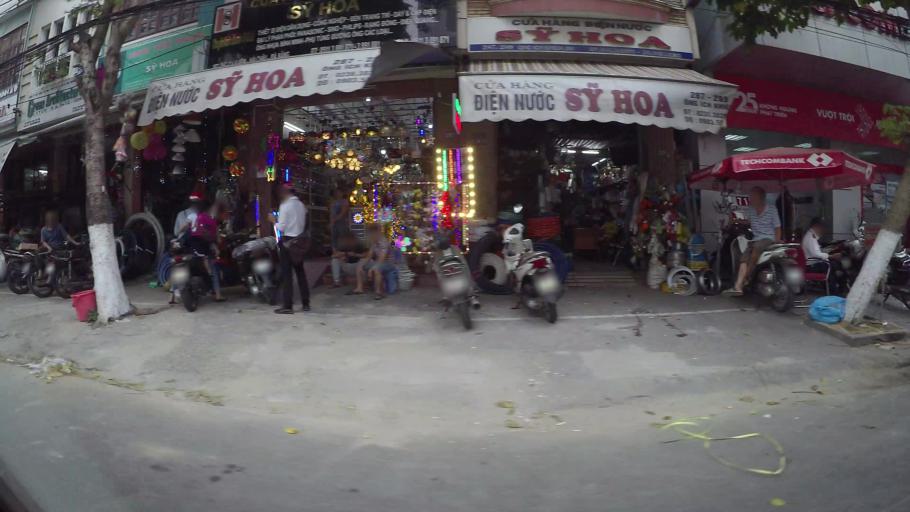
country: VN
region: Da Nang
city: Da Nang
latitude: 16.0663
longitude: 108.2143
